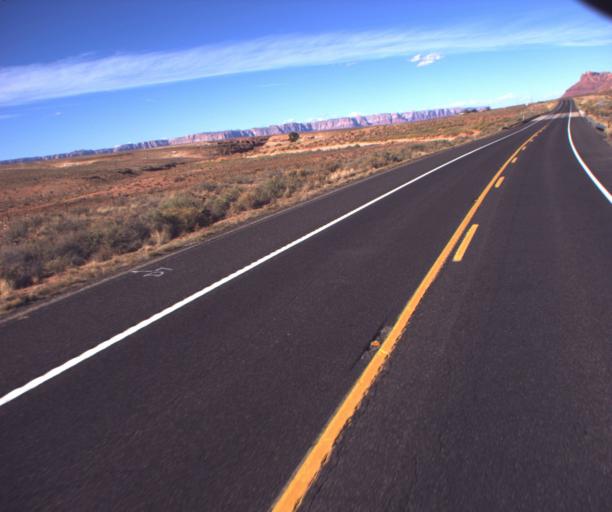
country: US
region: Arizona
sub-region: Coconino County
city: LeChee
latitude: 36.5977
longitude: -111.6570
